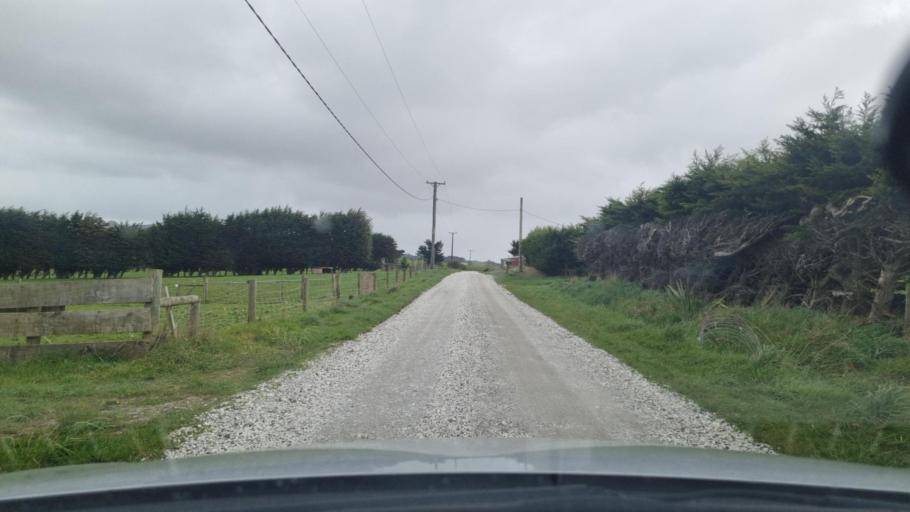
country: NZ
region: Southland
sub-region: Invercargill City
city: Bluff
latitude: -46.5419
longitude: 168.2930
